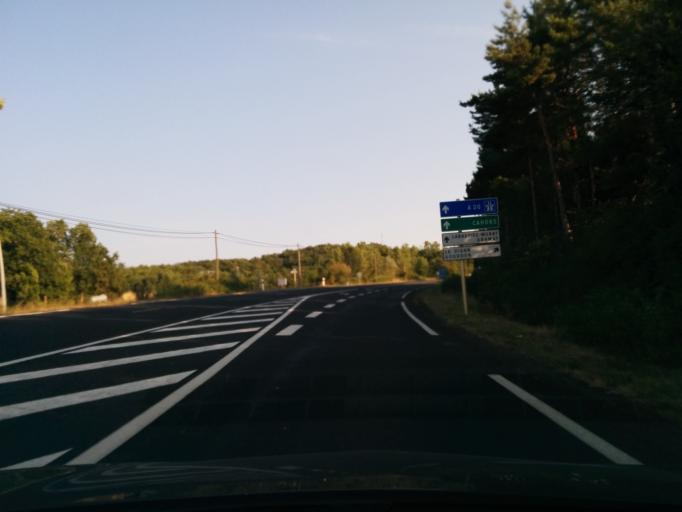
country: FR
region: Midi-Pyrenees
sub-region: Departement du Lot
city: Le Vigan
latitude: 44.7720
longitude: 1.4768
